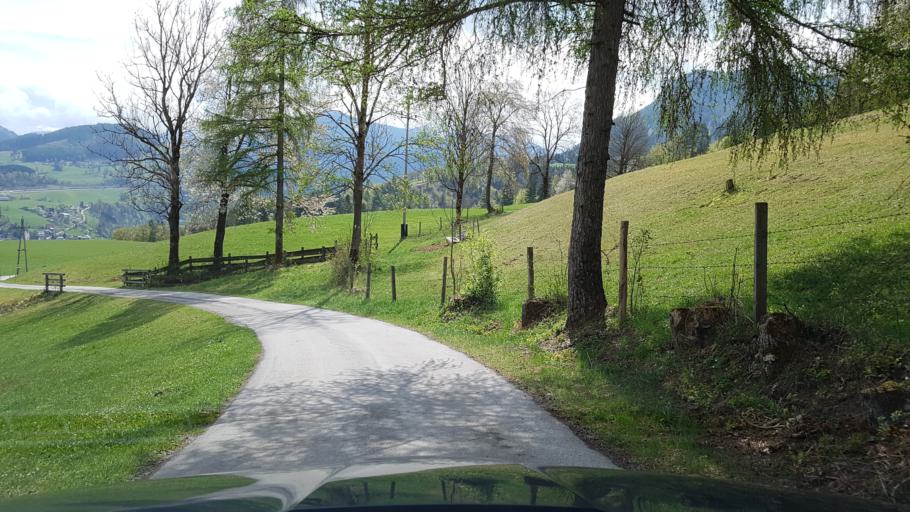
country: AT
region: Salzburg
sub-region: Politischer Bezirk Sankt Johann im Pongau
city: Werfen
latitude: 47.4643
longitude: 13.1859
